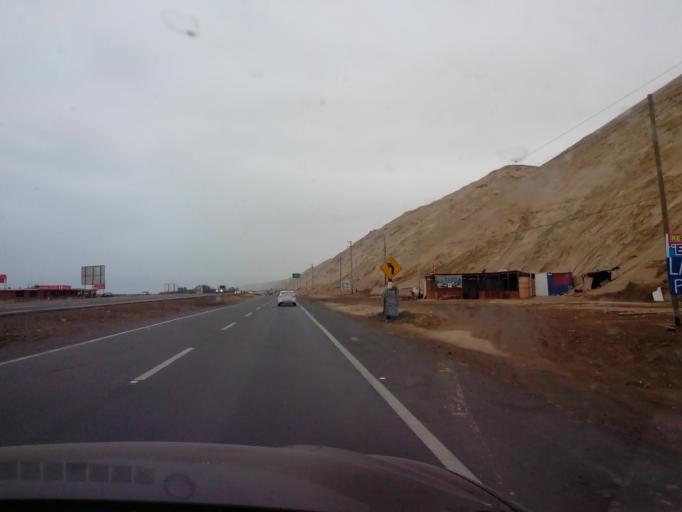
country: PE
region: Ica
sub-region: Provincia de Chincha
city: San Pedro
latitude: -13.3975
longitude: -76.1965
